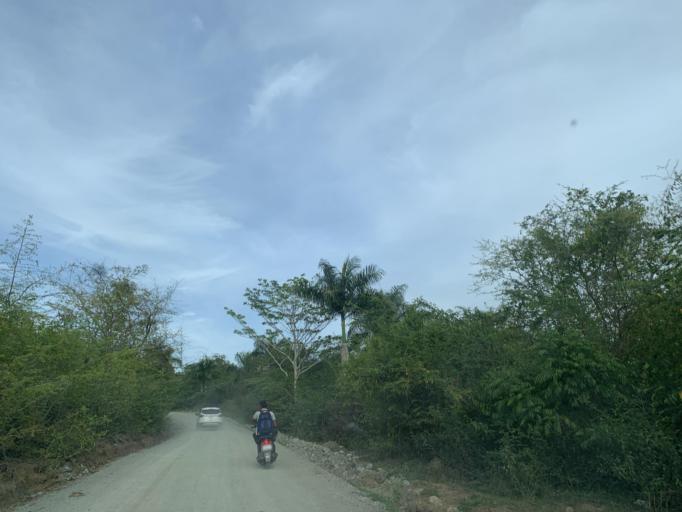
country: DO
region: Santiago
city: Pedro Garcia
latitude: 19.6982
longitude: -70.6159
